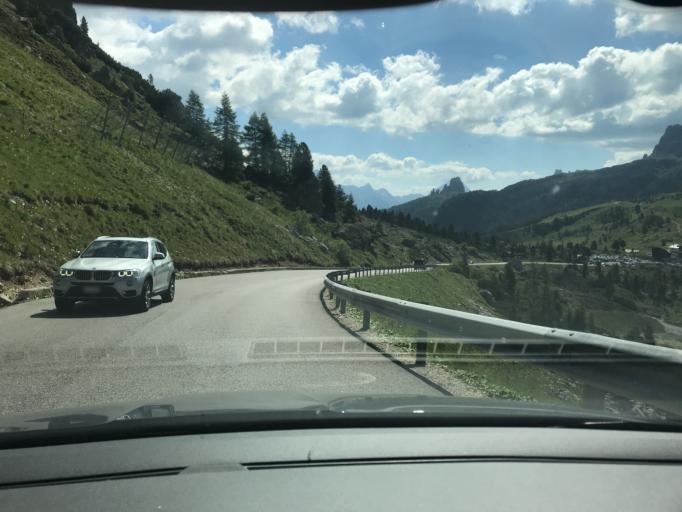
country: IT
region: Veneto
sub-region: Provincia di Belluno
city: Livinallongo del Col di Lana
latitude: 46.5225
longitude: 12.0025
